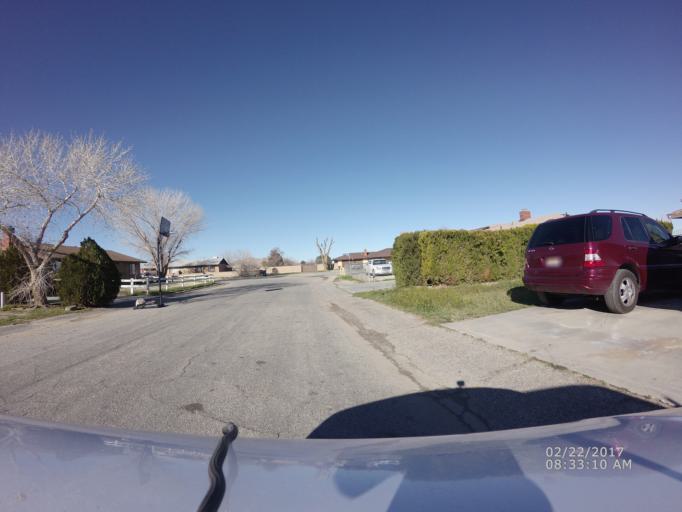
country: US
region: California
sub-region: Los Angeles County
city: Lake Los Angeles
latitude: 34.6370
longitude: -117.8516
